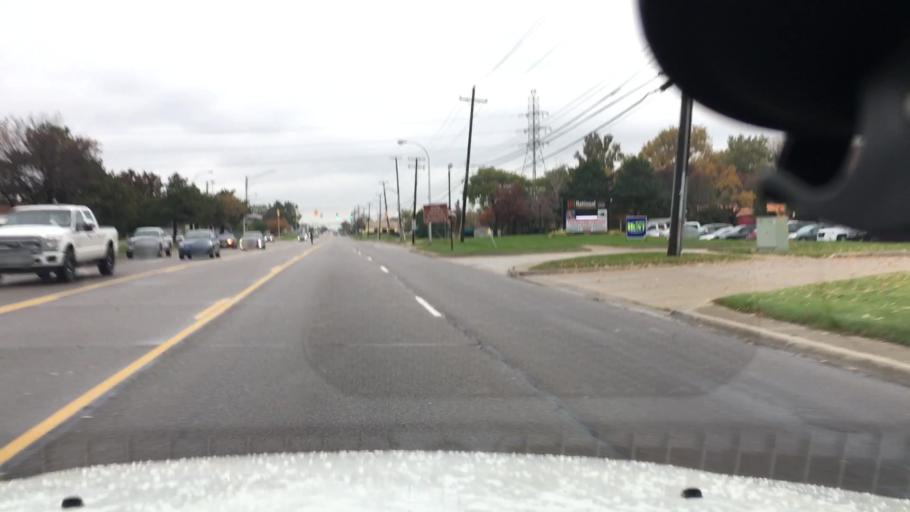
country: US
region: Michigan
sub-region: Oakland County
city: Madison Heights
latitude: 42.5072
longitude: -83.1058
